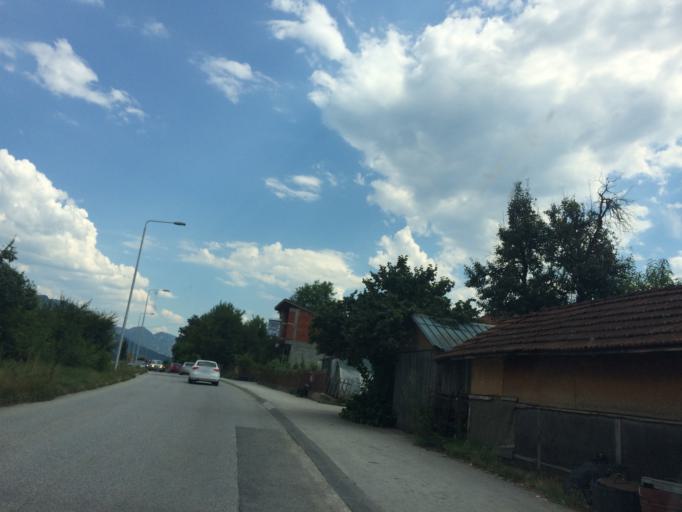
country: RS
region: Central Serbia
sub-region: Zlatiborski Okrug
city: Prijepolje
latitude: 43.3629
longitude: 19.6323
